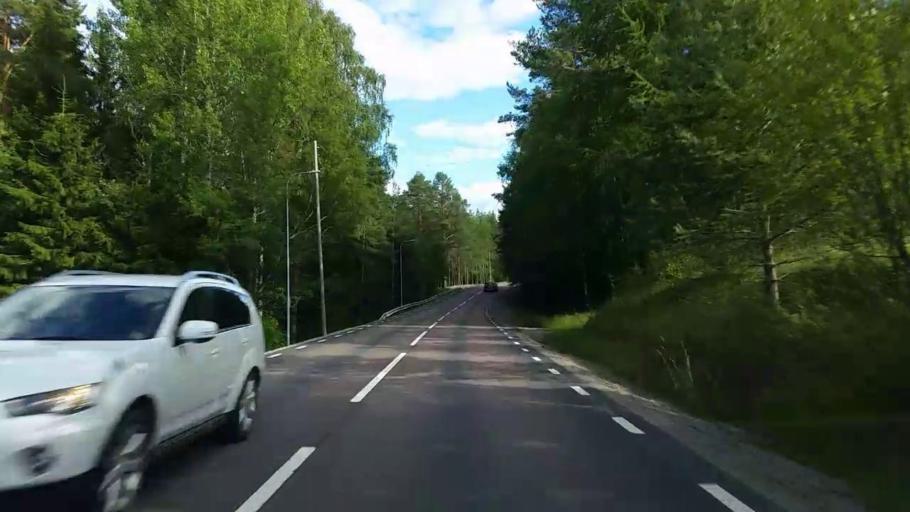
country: SE
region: Gaevleborg
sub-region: Ljusdals Kommun
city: Ljusdal
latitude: 61.8706
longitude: 15.9801
